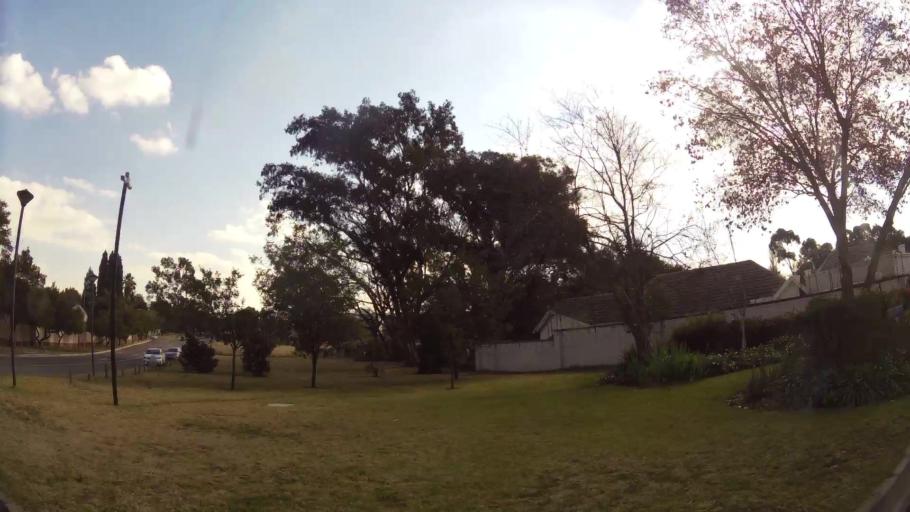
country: ZA
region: Gauteng
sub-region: City of Johannesburg Metropolitan Municipality
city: Diepsloot
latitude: -26.0314
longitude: 28.0166
